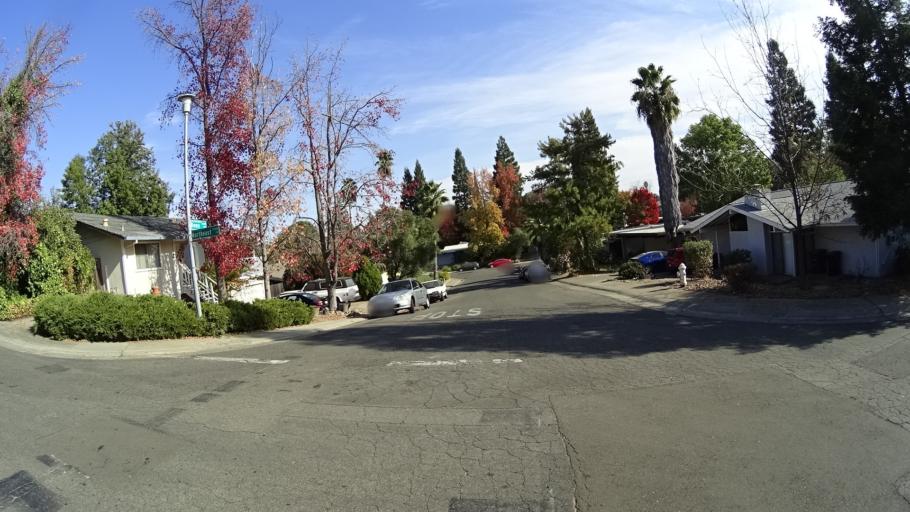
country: US
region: California
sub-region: Sacramento County
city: Fair Oaks
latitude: 38.6685
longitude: -121.2822
